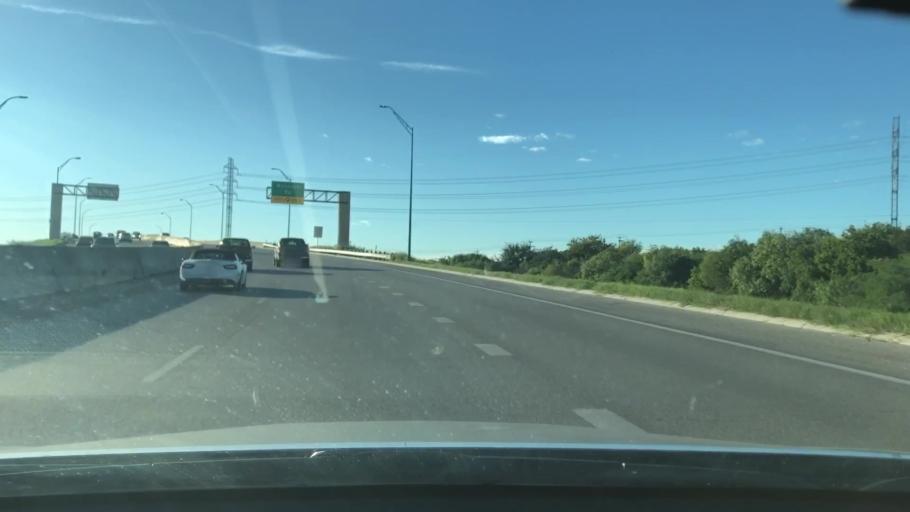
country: US
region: Texas
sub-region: Bexar County
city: Windcrest
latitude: 29.5461
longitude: -98.4322
